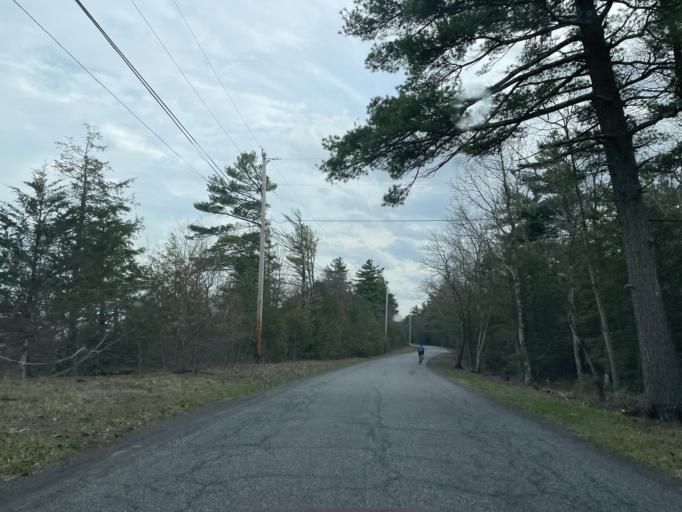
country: US
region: New York
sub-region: Ulster County
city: Manorville
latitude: 42.1308
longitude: -74.0403
